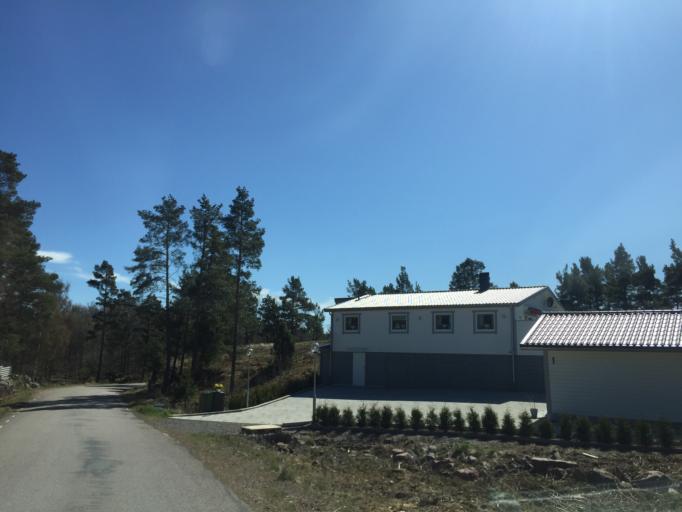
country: SE
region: Kalmar
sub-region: Oskarshamns Kommun
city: Oskarshamn
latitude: 57.2319
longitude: 16.4811
